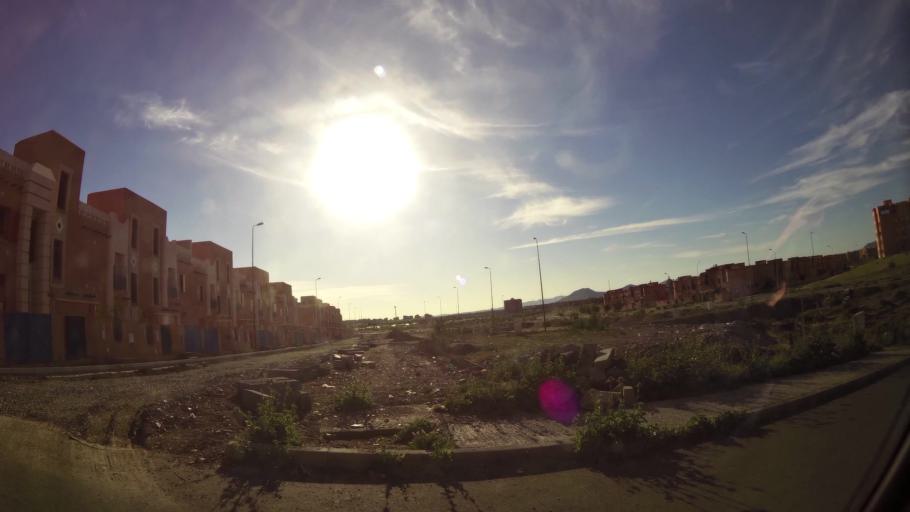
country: MA
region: Marrakech-Tensift-Al Haouz
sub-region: Marrakech
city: Marrakesh
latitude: 31.7548
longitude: -8.1028
